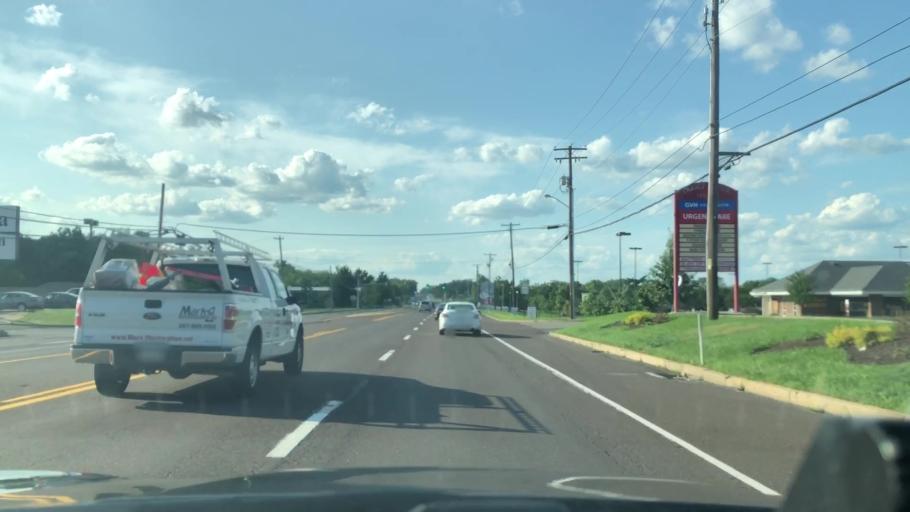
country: US
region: Pennsylvania
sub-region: Bucks County
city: Quakertown
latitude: 40.4232
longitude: -75.3468
